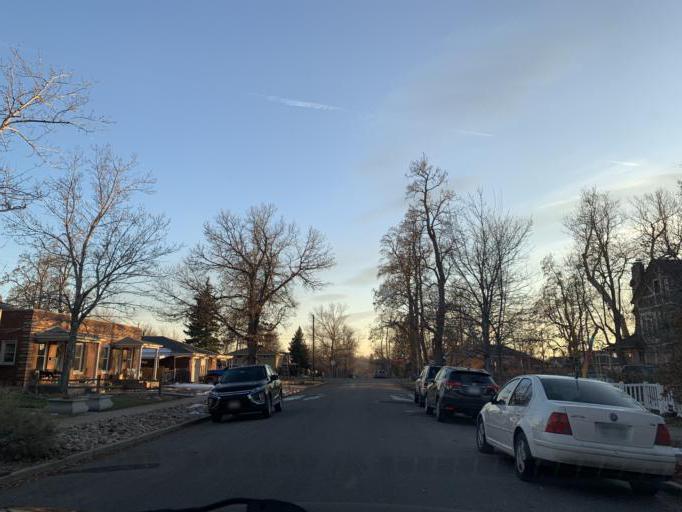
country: US
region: Colorado
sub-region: Adams County
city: Berkley
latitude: 39.7864
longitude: -105.0428
